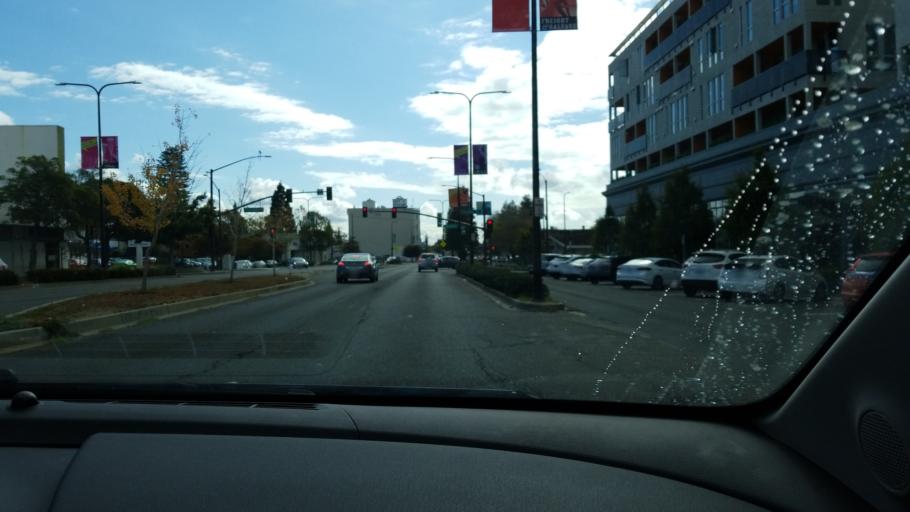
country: US
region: California
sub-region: Alameda County
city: Berkeley
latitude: 37.8620
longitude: -122.2673
